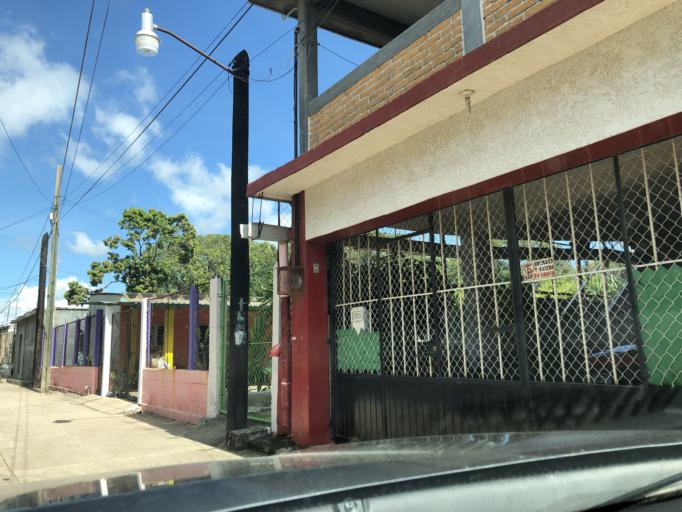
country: MX
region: Oaxaca
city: San Jeronimo Ixtepec
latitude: 16.5581
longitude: -95.1029
